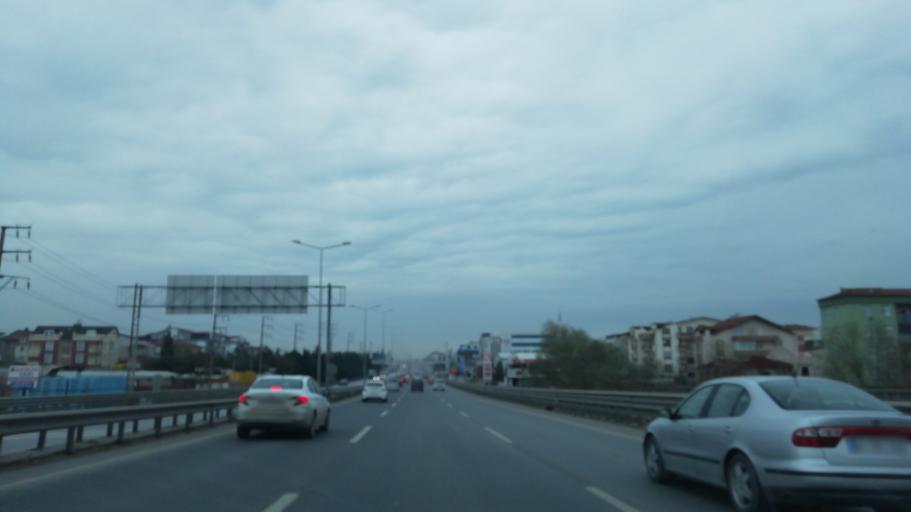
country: TR
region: Kocaeli
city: Derince
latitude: 40.7577
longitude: 29.8002
